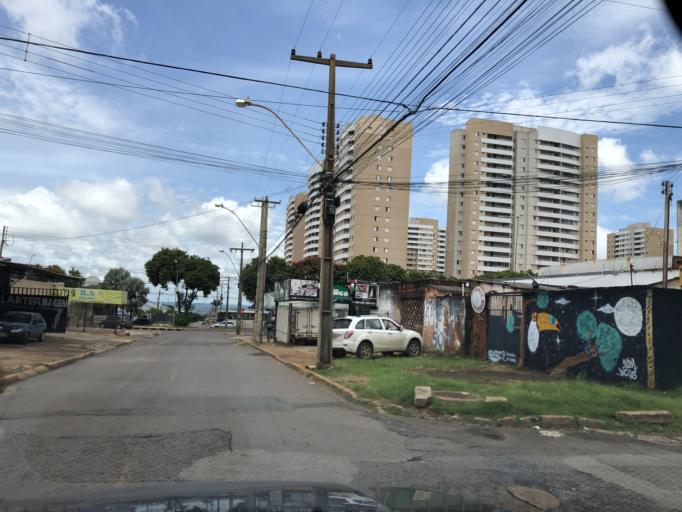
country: BR
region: Federal District
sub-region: Brasilia
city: Brasilia
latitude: -15.8183
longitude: -48.1207
